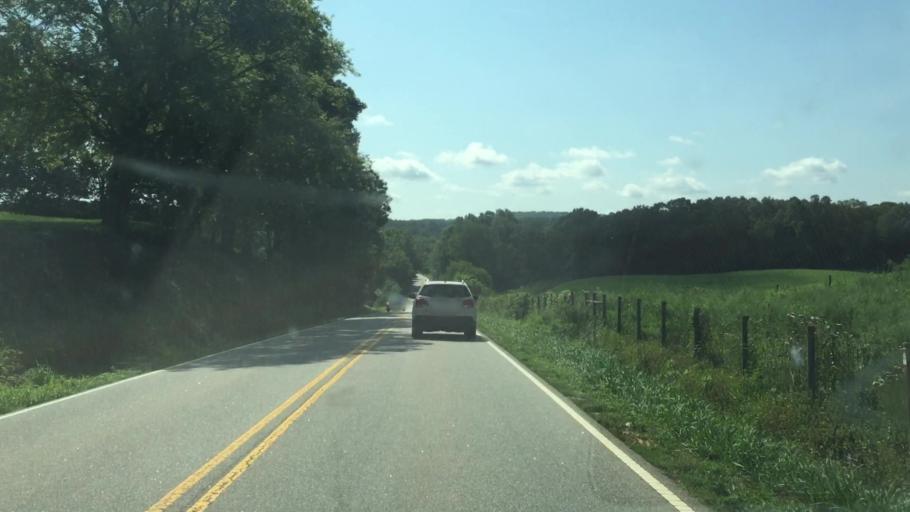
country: US
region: North Carolina
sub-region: Anson County
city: Burnsville
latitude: 35.0941
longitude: -80.3030
